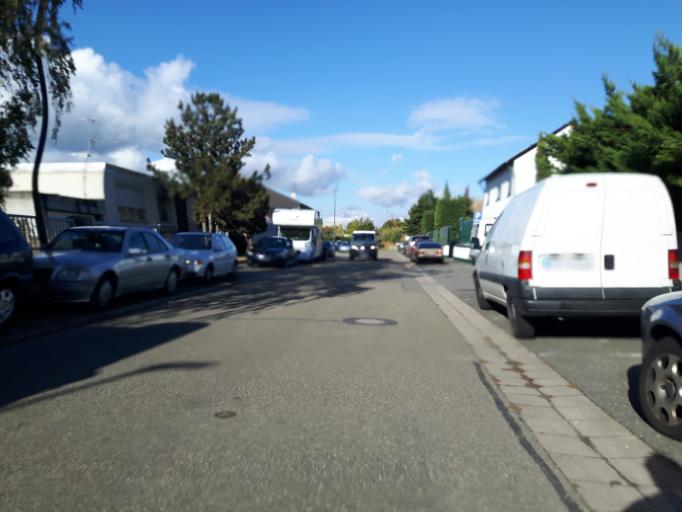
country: DE
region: Rheinland-Pfalz
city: Erpolzheim
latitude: 49.4713
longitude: 8.2054
